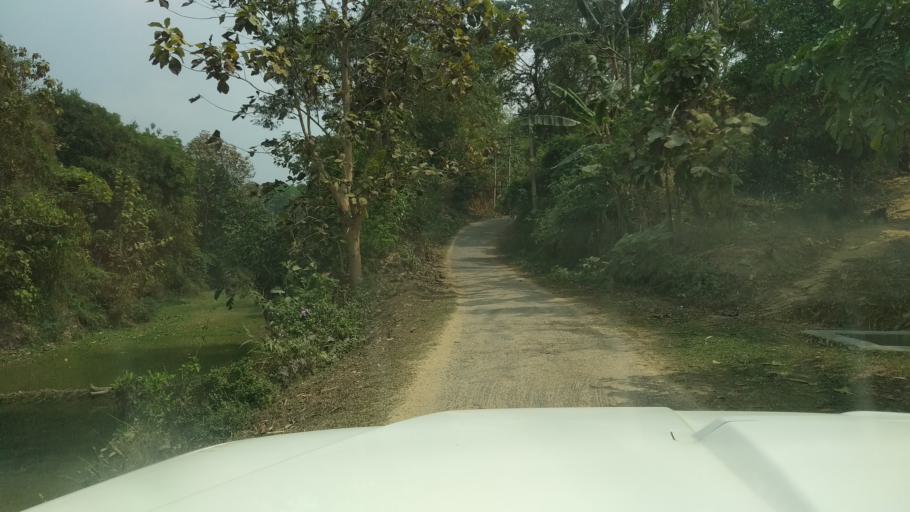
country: IN
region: Tripura
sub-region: West Tripura
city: Sonamura
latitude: 23.4270
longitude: 91.3226
